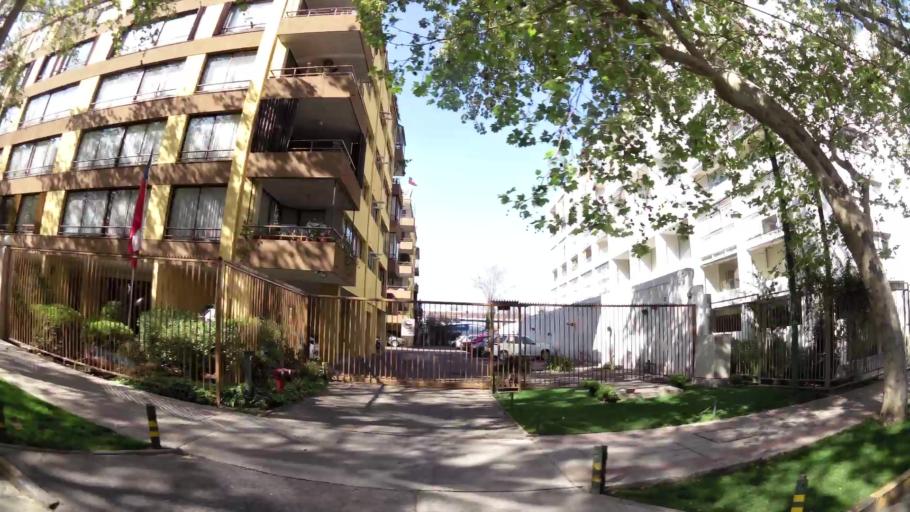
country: CL
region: Santiago Metropolitan
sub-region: Provincia de Santiago
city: Santiago
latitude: -33.4413
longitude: -70.6224
